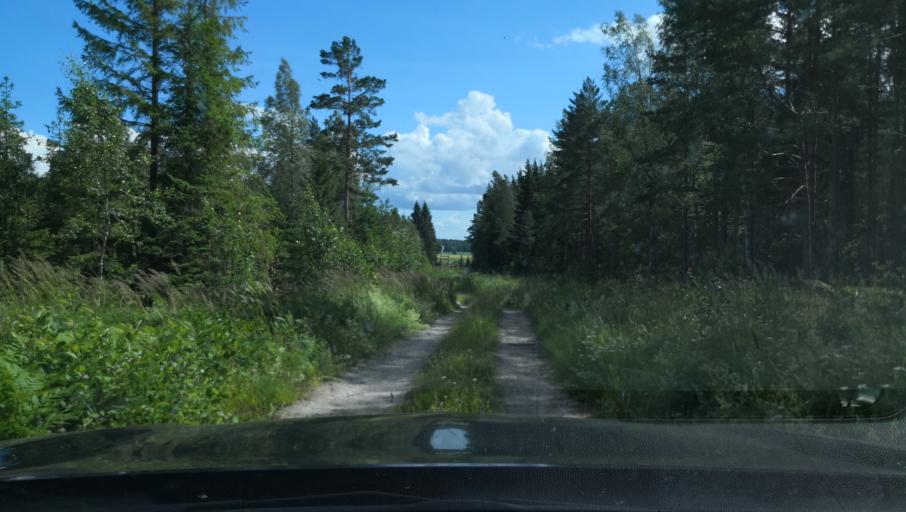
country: SE
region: Vaestmanland
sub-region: Kungsors Kommun
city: Kungsoer
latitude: 59.3337
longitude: 16.0641
